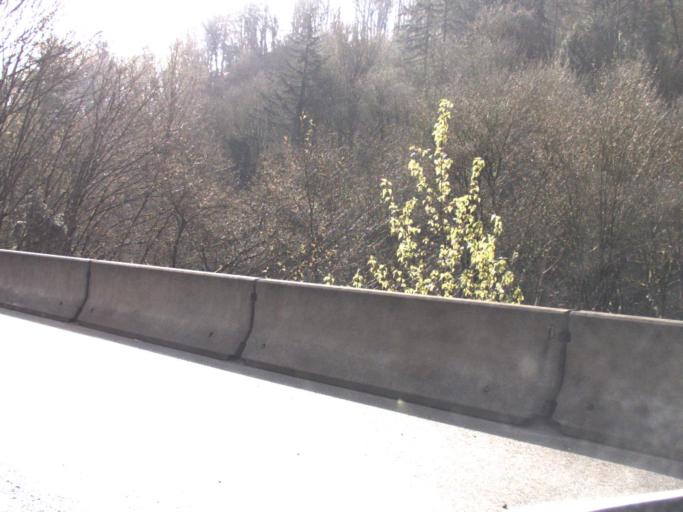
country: US
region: Washington
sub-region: King County
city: Algona
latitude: 47.3038
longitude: -122.2660
